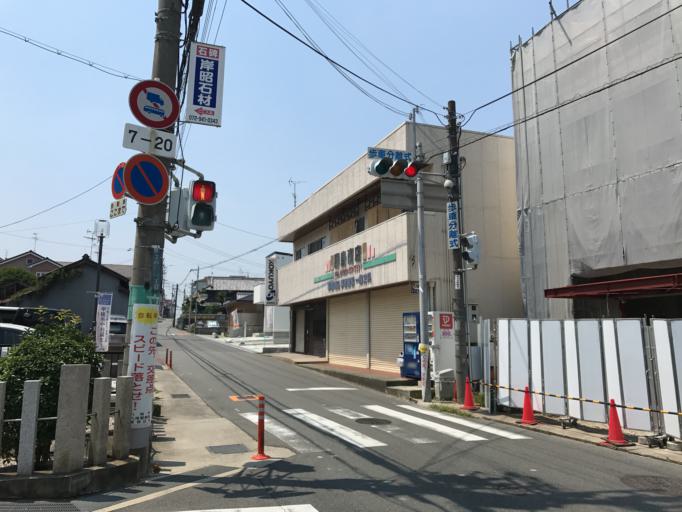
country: JP
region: Osaka
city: Kashihara
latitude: 34.6099
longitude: 135.6325
